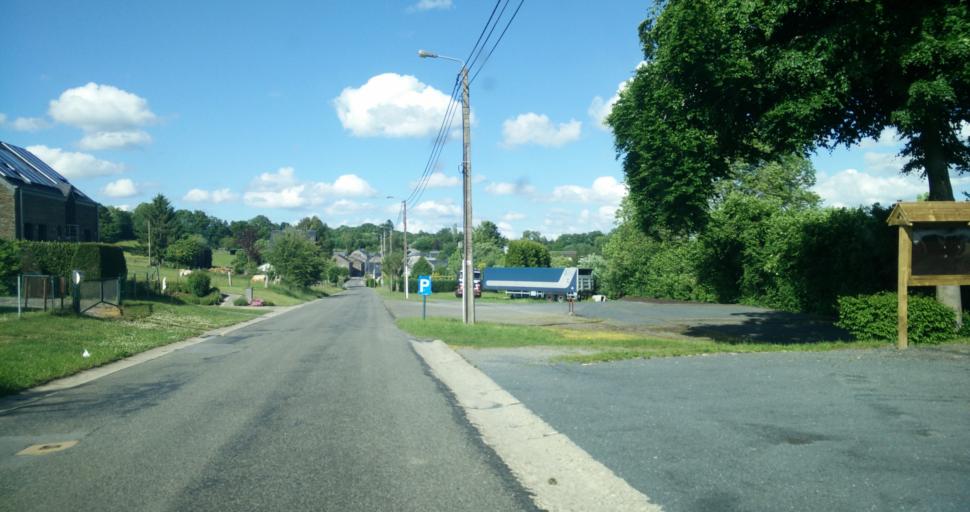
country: BE
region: Wallonia
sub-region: Province du Luxembourg
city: Houffalize
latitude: 50.1690
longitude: 5.7695
